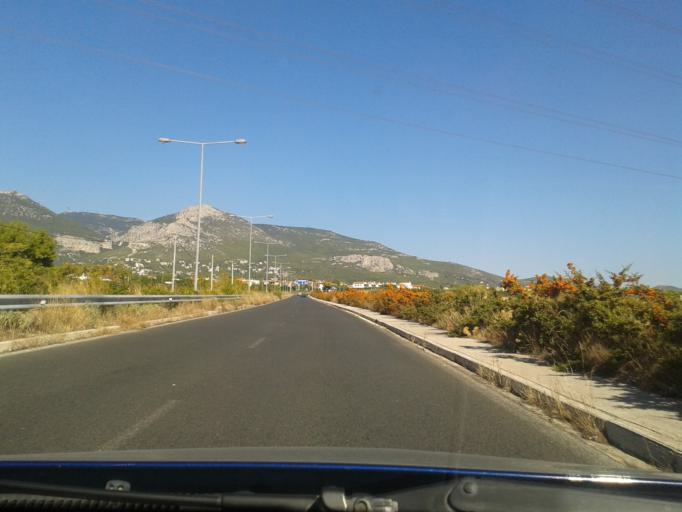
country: GR
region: Attica
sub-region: Nomarchia Anatolikis Attikis
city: Thrakomakedones
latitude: 38.1143
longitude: 23.7625
